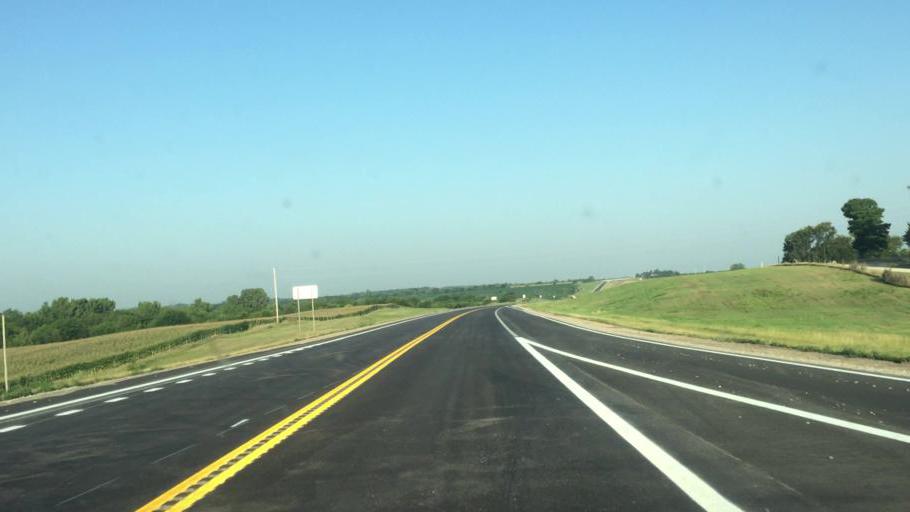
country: US
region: Kansas
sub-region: Doniphan County
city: Highland
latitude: 39.8417
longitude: -95.3637
